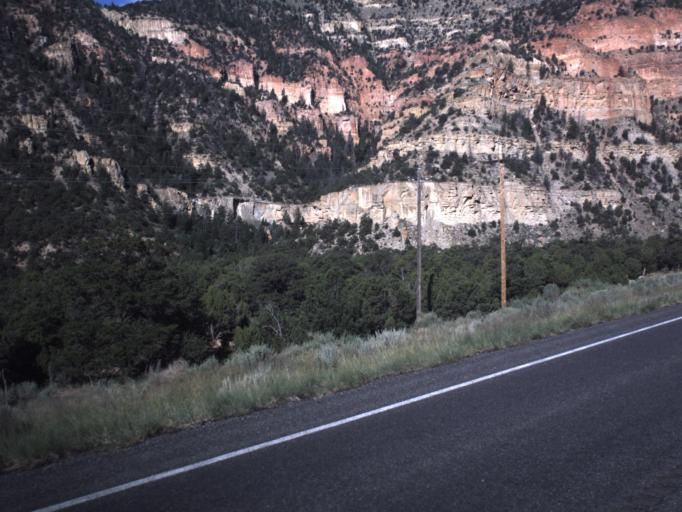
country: US
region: Utah
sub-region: Emery County
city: Huntington
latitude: 39.3948
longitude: -111.1050
